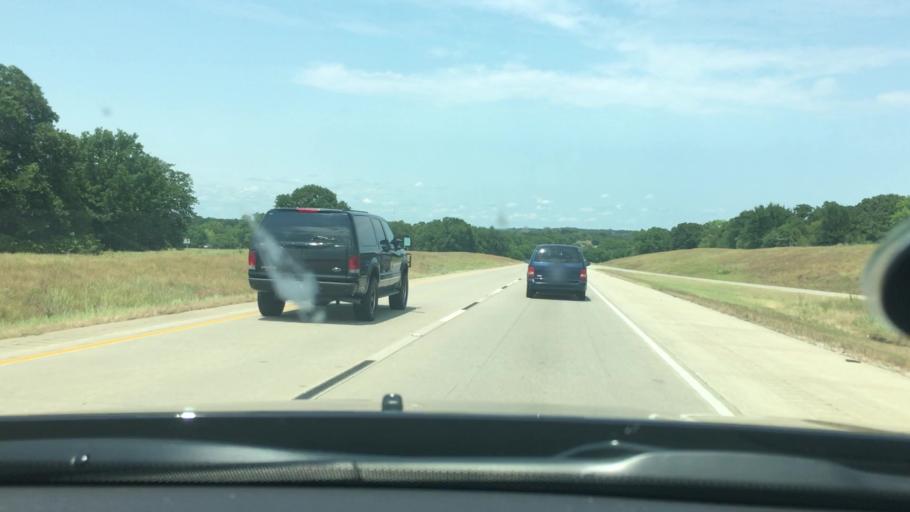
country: US
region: Oklahoma
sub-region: Love County
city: Marietta
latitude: 34.0284
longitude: -97.1476
